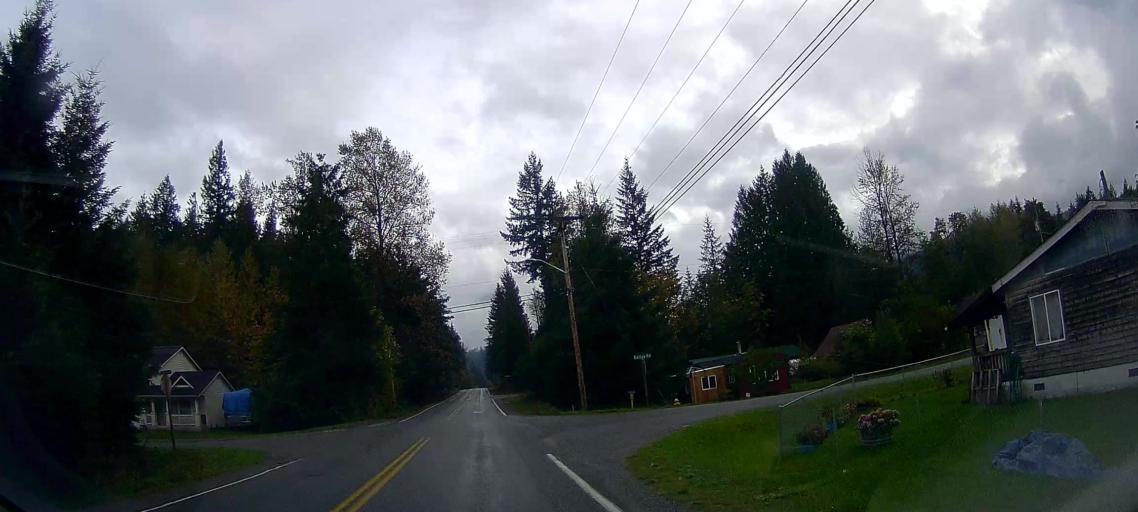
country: US
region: Washington
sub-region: Snohomish County
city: Darrington
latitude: 48.5348
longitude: -121.7661
